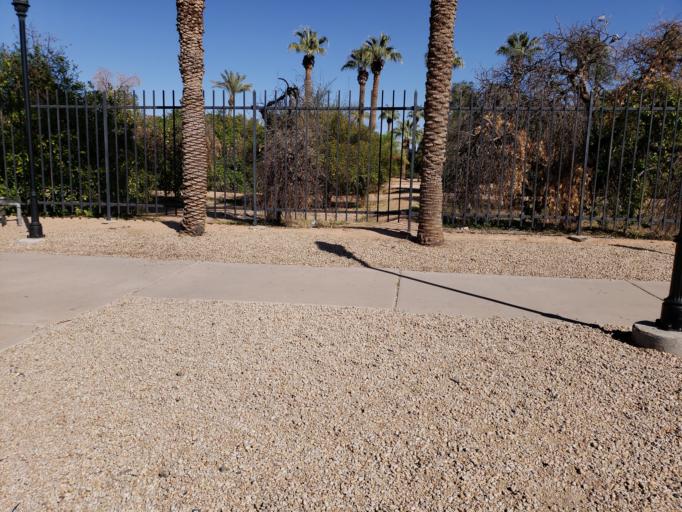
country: US
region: Arizona
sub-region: Maricopa County
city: Glendale
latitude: 33.5760
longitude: -112.1895
